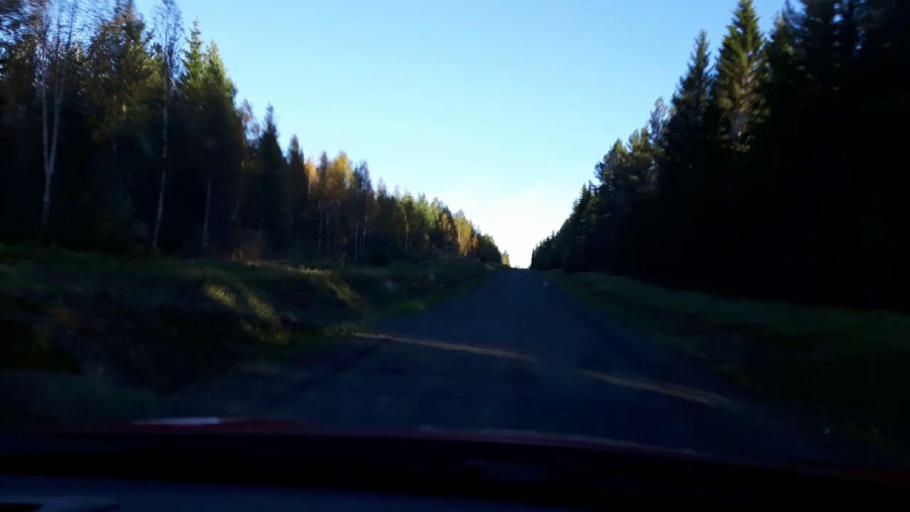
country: SE
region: Jaemtland
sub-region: OEstersunds Kommun
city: Lit
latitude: 63.5994
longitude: 14.8157
